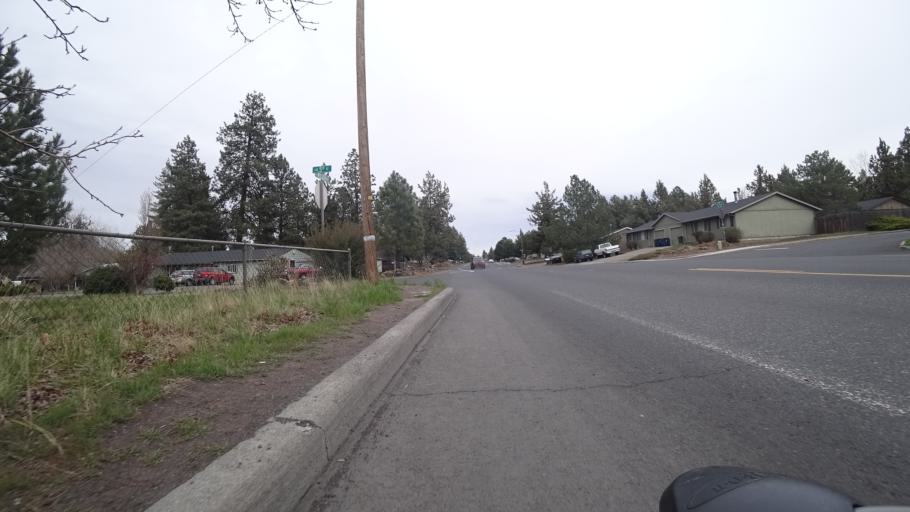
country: US
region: Oregon
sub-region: Deschutes County
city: Bend
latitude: 44.0443
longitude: -121.2990
